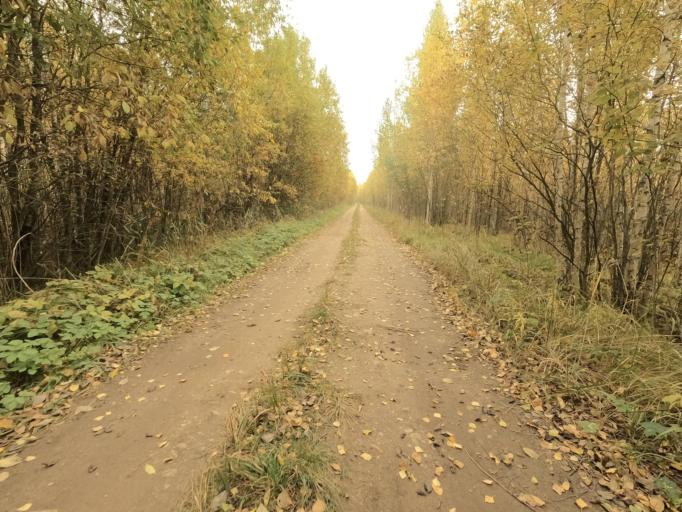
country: RU
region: Novgorod
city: Pankovka
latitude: 58.8753
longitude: 30.8763
